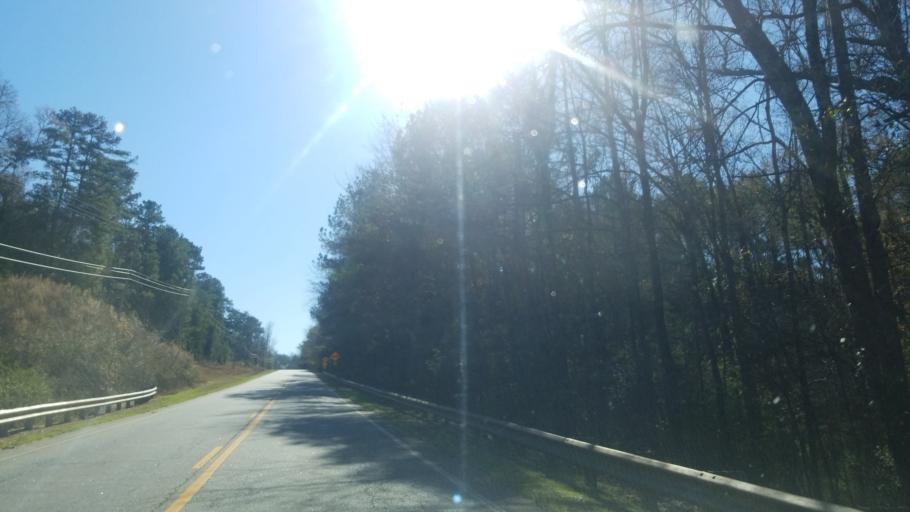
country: US
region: Alabama
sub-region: Lee County
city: Smiths Station
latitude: 32.5849
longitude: -85.0209
